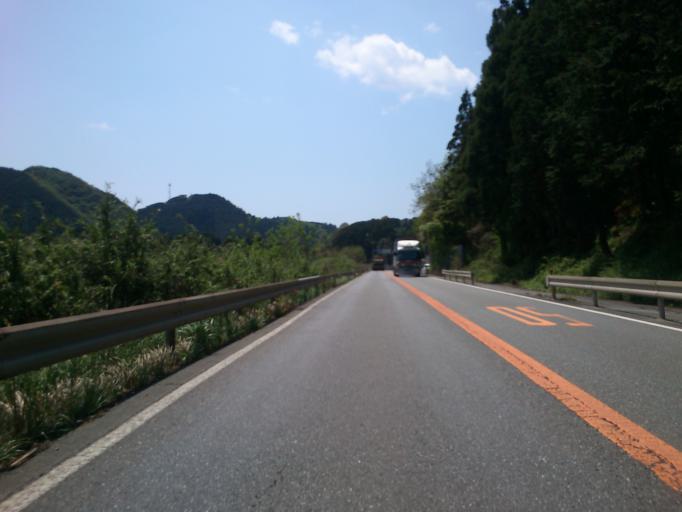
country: JP
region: Kyoto
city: Fukuchiyama
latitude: 35.3221
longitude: 135.0142
